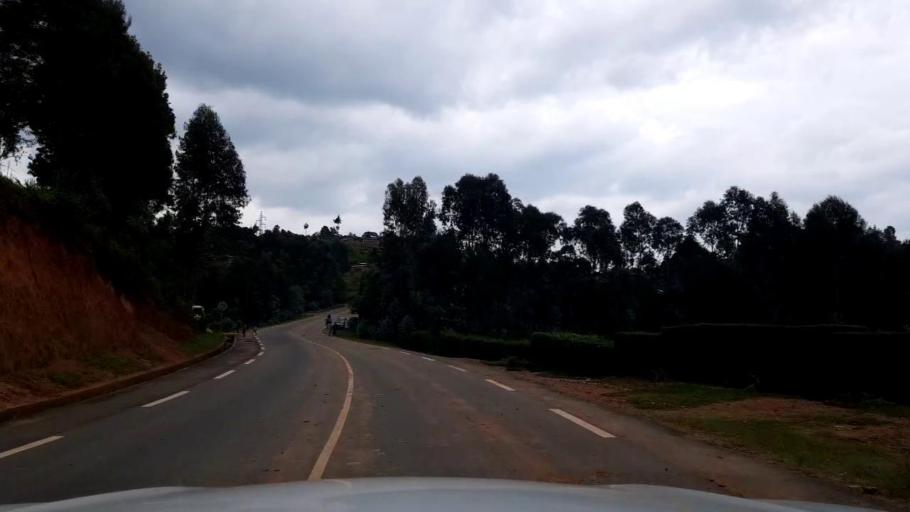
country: RW
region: Western Province
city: Kibuye
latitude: -1.8791
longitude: 29.3513
